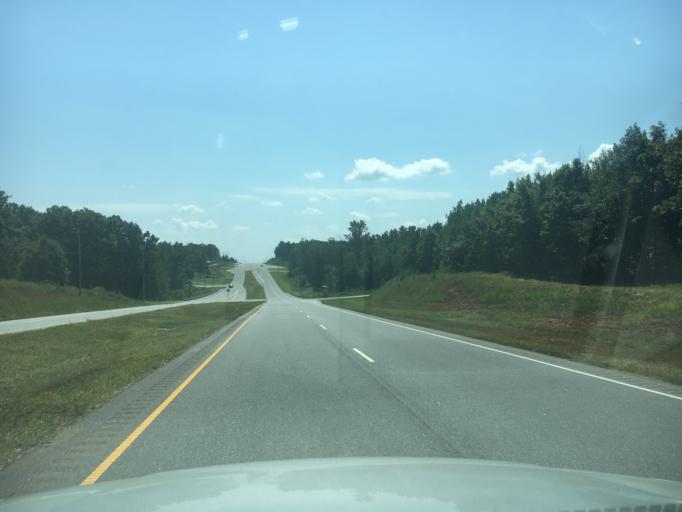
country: US
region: North Carolina
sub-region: Rutherford County
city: Spindale
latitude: 35.3040
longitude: -81.9195
